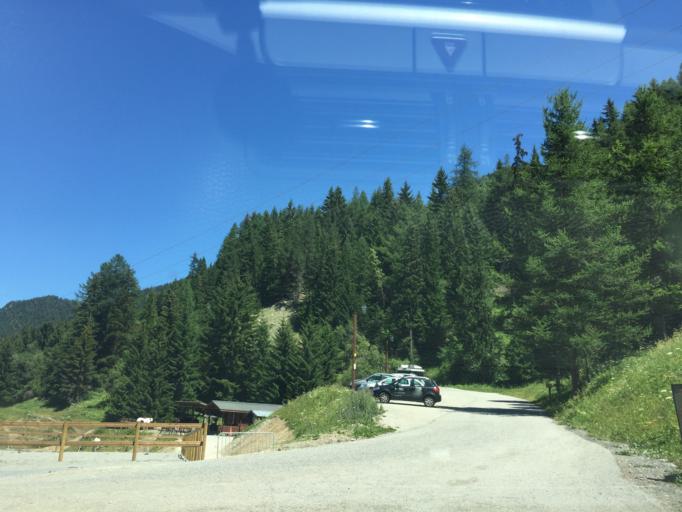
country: FR
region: Rhone-Alpes
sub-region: Departement de la Savoie
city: Modane
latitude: 45.1669
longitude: 6.6494
